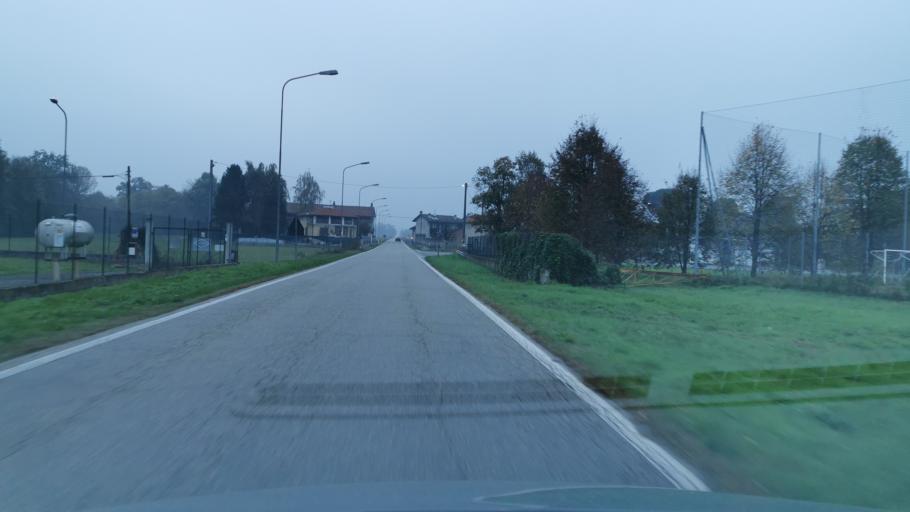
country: IT
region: Piedmont
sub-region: Provincia di Torino
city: Lusiglie
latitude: 45.3163
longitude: 7.7588
